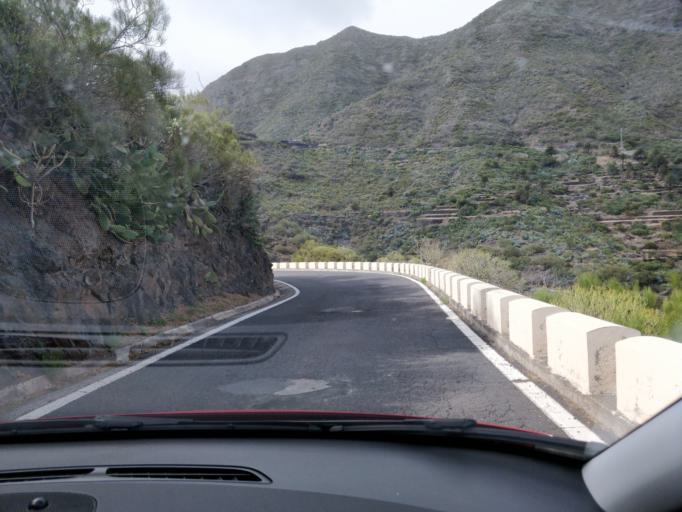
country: ES
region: Canary Islands
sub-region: Provincia de Santa Cruz de Tenerife
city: Santiago del Teide
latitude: 28.3089
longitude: -16.8458
